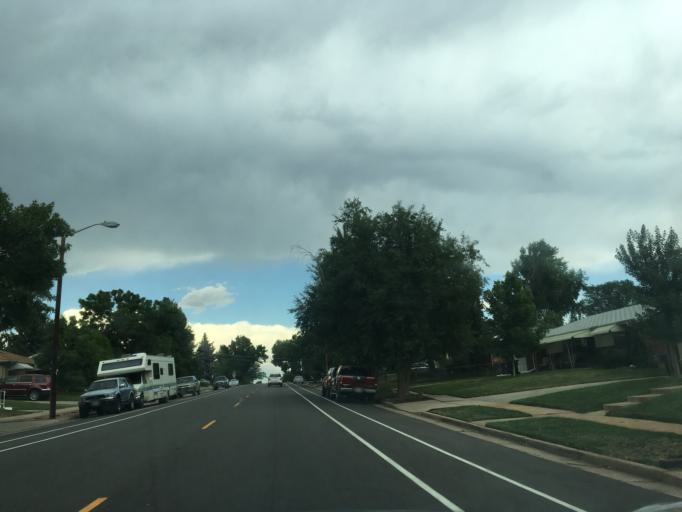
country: US
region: Colorado
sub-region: Arapahoe County
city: Sheridan
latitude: 39.6736
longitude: -105.0417
